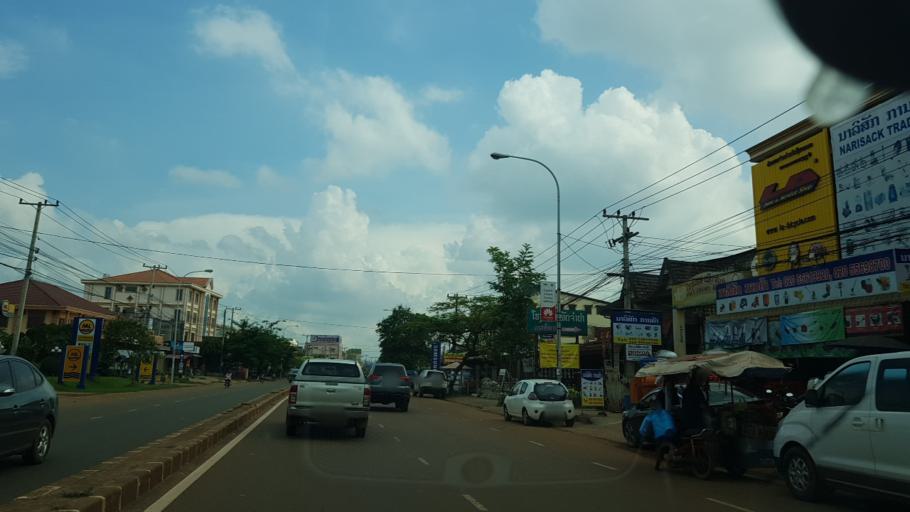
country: LA
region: Vientiane
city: Vientiane
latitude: 18.0241
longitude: 102.6516
